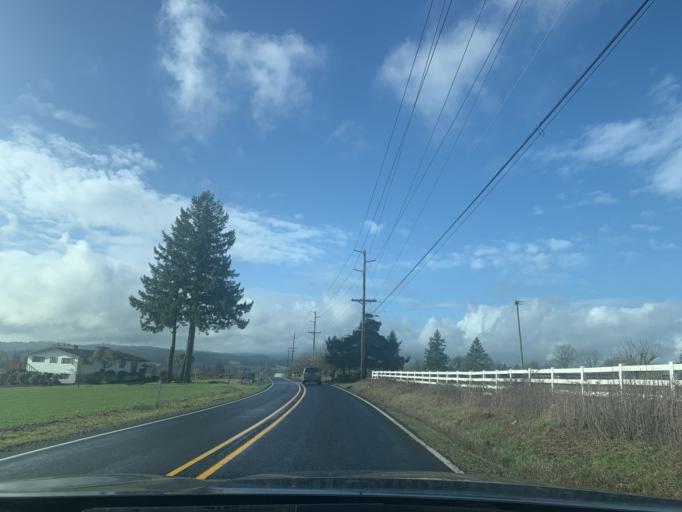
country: US
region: Oregon
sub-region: Washington County
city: King City
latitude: 45.4016
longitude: -122.8376
